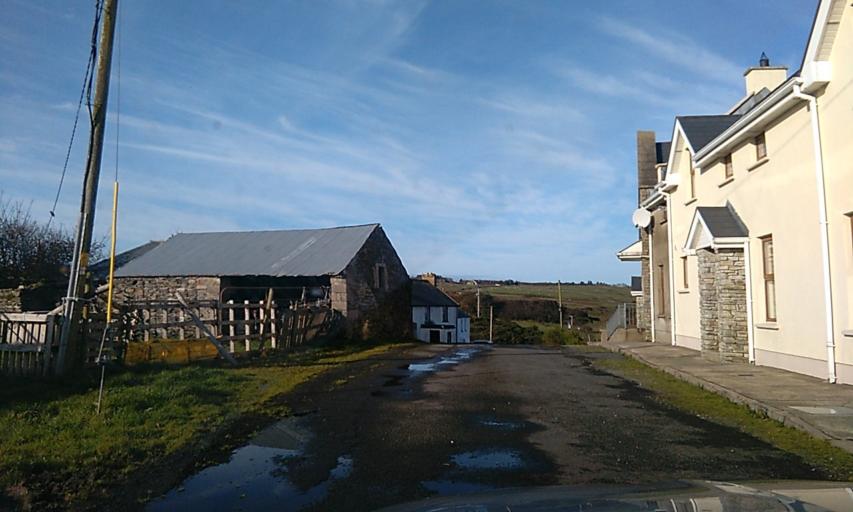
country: IE
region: Ulster
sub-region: County Donegal
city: Moville
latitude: 55.2694
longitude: -7.0661
